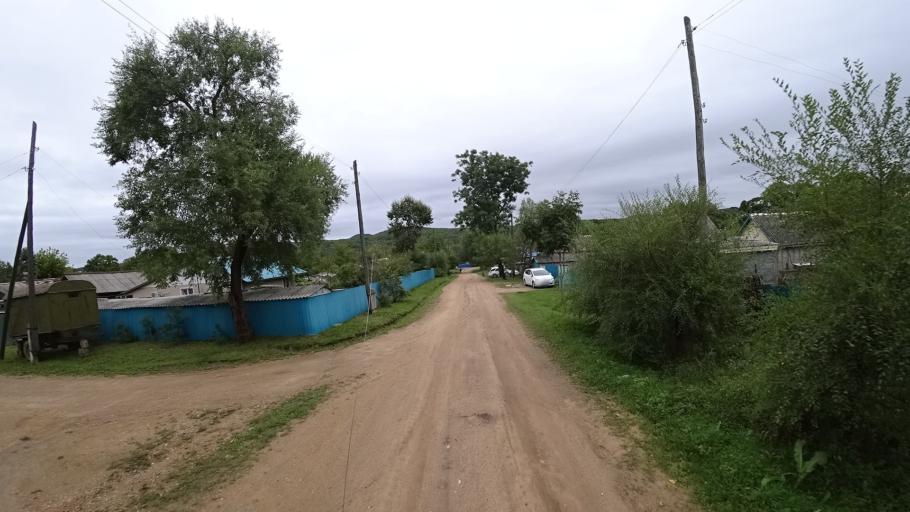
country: RU
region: Primorskiy
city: Rettikhovka
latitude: 44.1687
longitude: 132.7681
